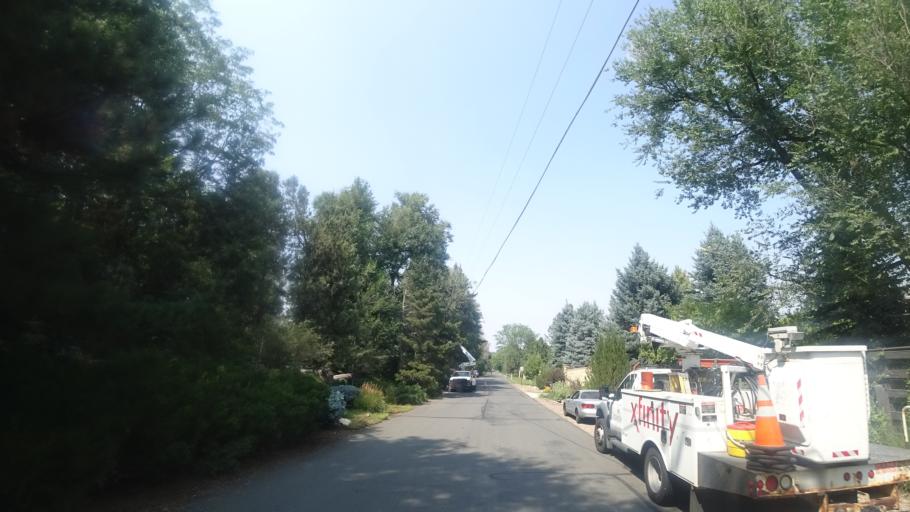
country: US
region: Colorado
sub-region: Arapahoe County
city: Cherry Hills Village
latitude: 39.6336
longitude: -104.9690
